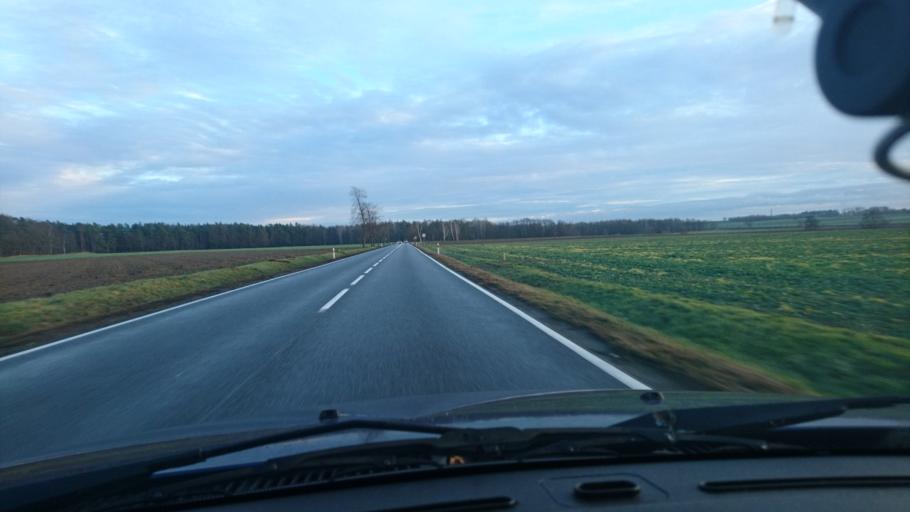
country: PL
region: Lodz Voivodeship
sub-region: Powiat wieruszowski
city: Boleslawiec
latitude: 51.1529
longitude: 18.1800
